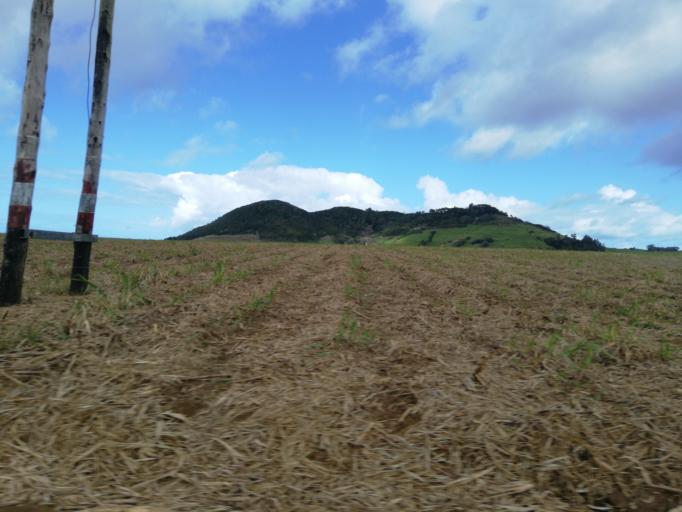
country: MU
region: Flacq
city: Grande Riviere Sud Est
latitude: -20.2815
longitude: 57.7569
